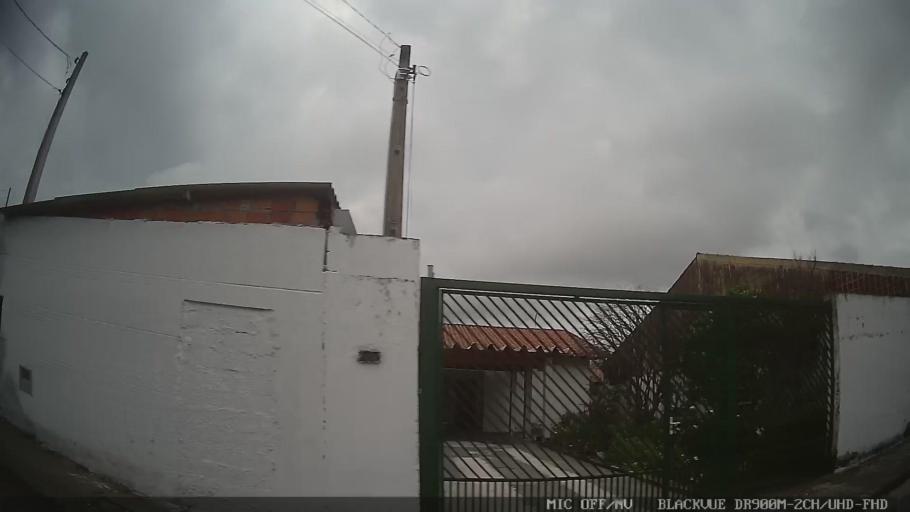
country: BR
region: Sao Paulo
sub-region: Mogi das Cruzes
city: Mogi das Cruzes
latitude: -23.5220
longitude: -46.2063
